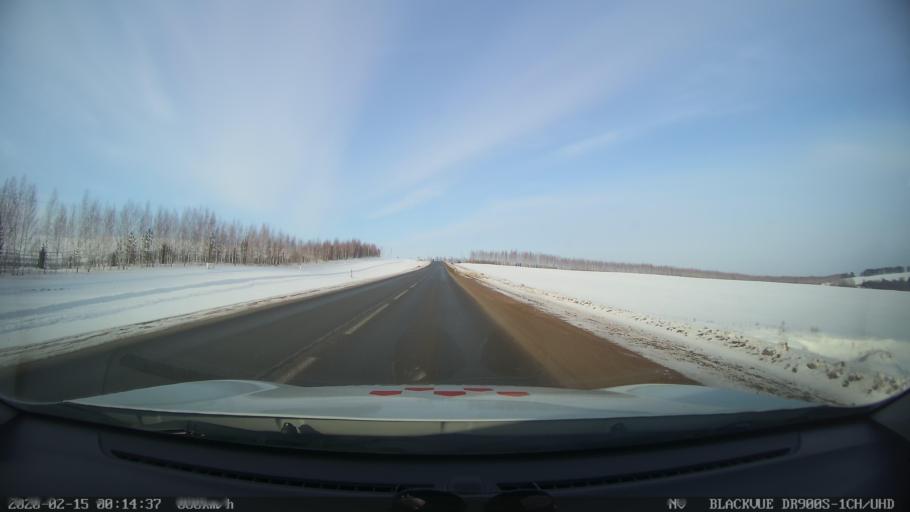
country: RU
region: Tatarstan
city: Stolbishchi
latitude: 55.4881
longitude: 49.0044
